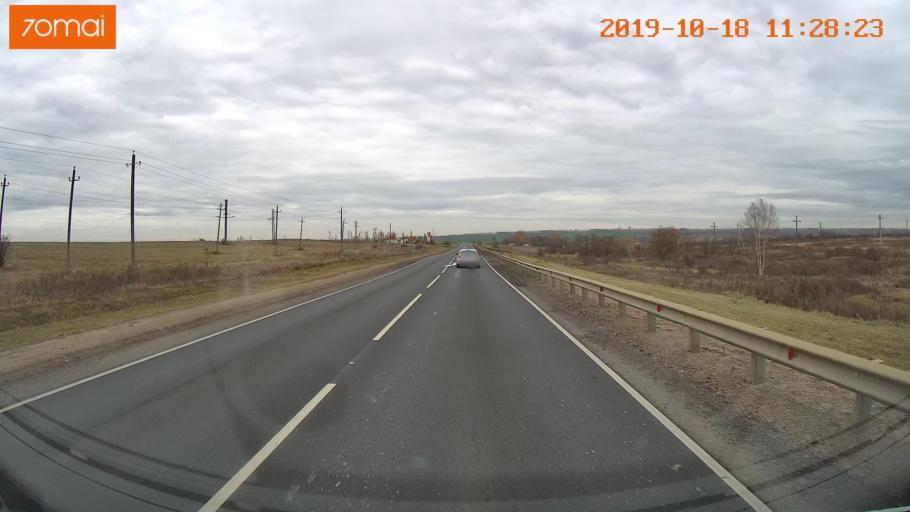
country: RU
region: Tula
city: Kimovsk
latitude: 54.1538
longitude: 38.6598
